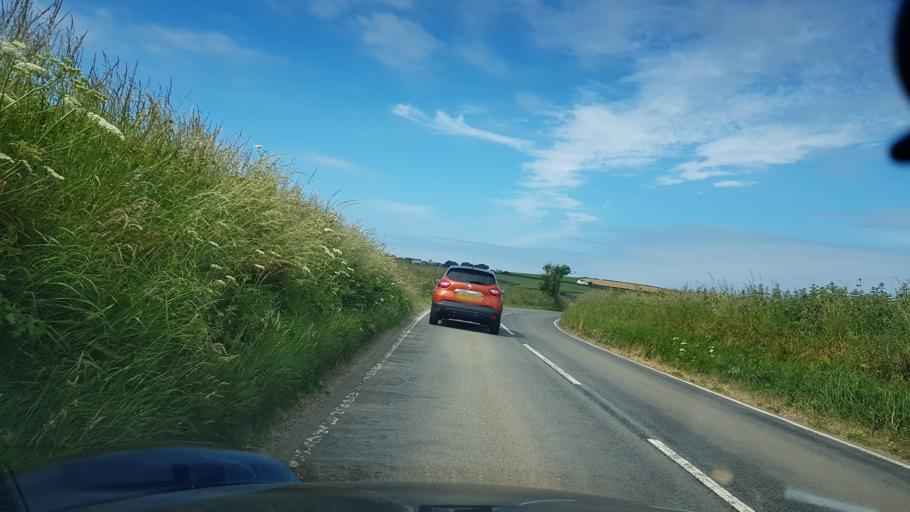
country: GB
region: Wales
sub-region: Pembrokeshire
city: Herbrandston
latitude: 51.7650
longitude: -5.0834
